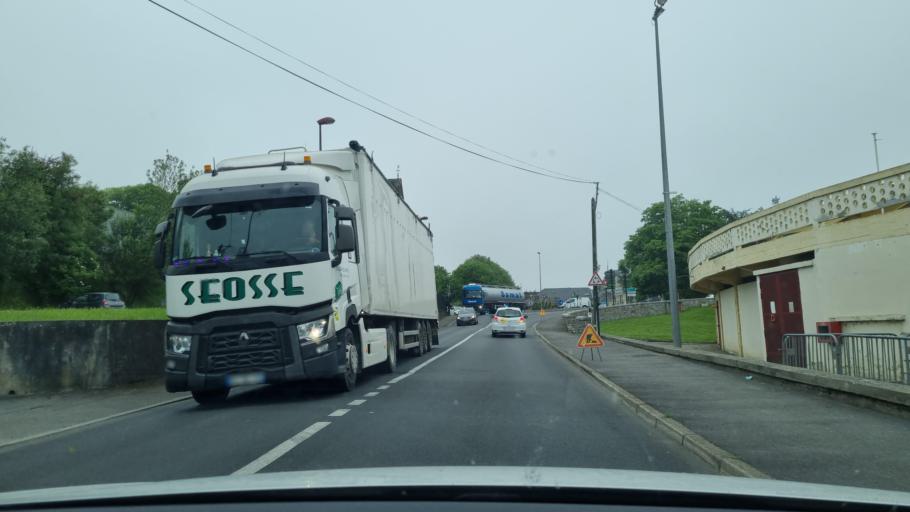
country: FR
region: Aquitaine
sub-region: Departement des Pyrenees-Atlantiques
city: Orthez
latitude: 43.4841
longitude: -0.7742
